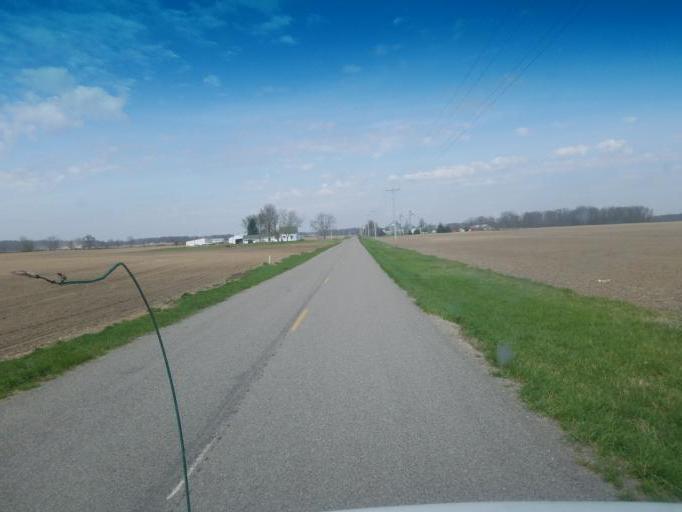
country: US
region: Ohio
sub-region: Logan County
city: Northwood
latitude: 40.4952
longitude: -83.6004
